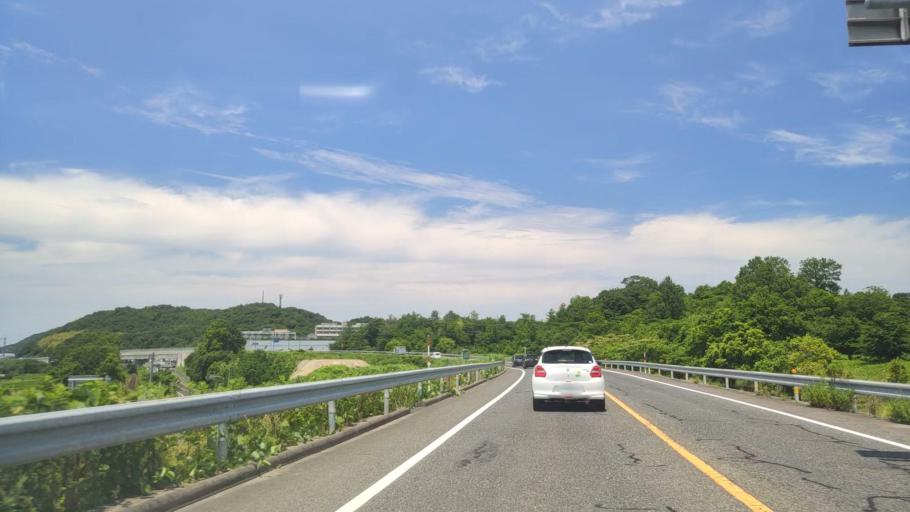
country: JP
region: Tottori
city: Tottori
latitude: 35.4447
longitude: 134.2559
